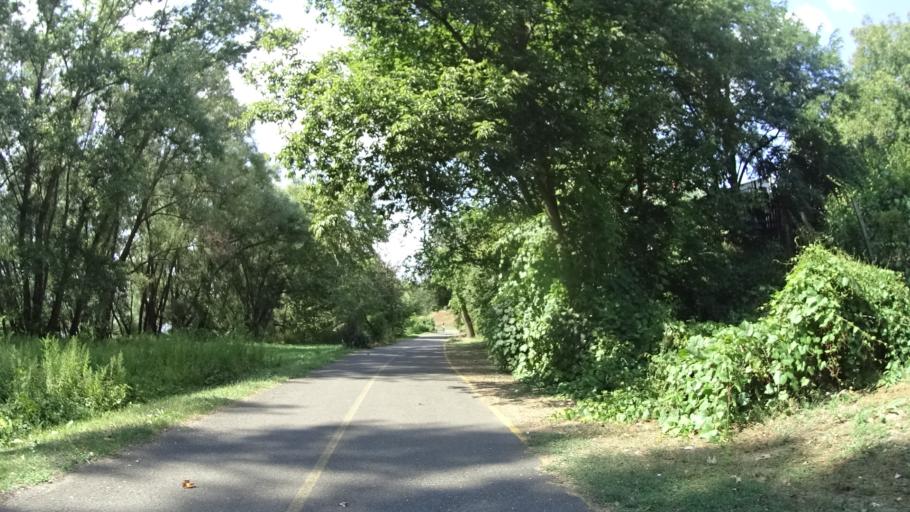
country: HU
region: Komarom-Esztergom
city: Pilismarot
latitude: 47.8053
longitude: 18.9043
